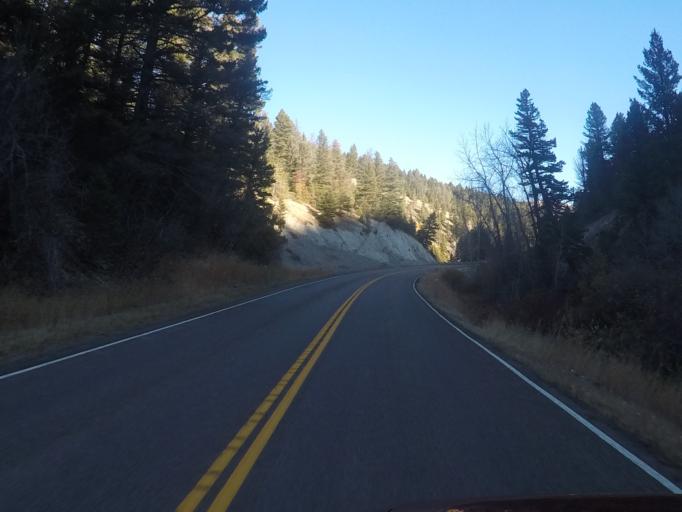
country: US
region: Montana
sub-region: Meagher County
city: White Sulphur Springs
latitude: 46.3538
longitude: -111.1320
